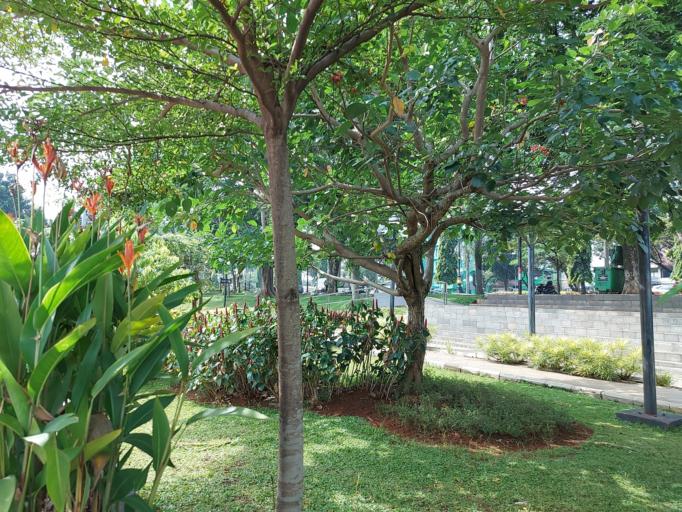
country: ID
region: West Java
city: Cibinong
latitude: -6.4808
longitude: 106.8270
